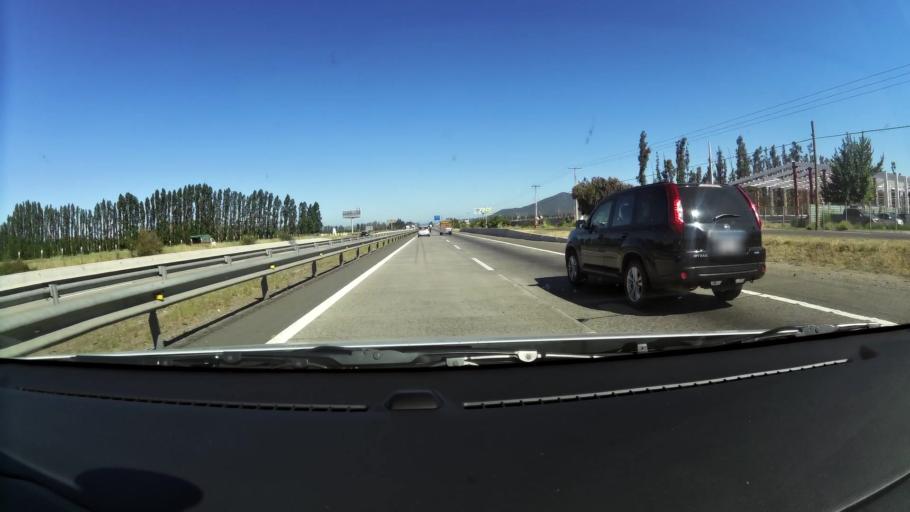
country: CL
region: Valparaiso
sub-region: Provincia de Marga Marga
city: Villa Alemana
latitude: -33.3533
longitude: -71.3379
